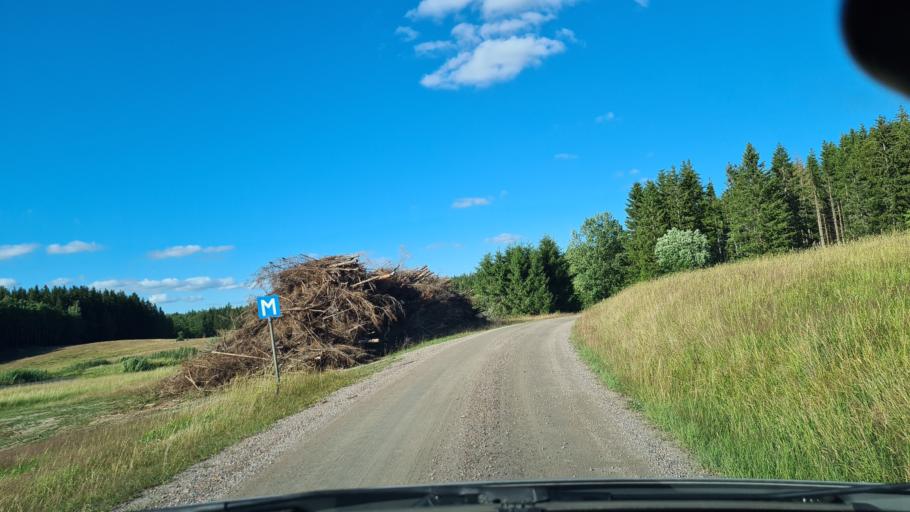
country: SE
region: Soedermanland
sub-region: Nykopings Kommun
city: Stigtomta
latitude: 58.9253
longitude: 16.8913
